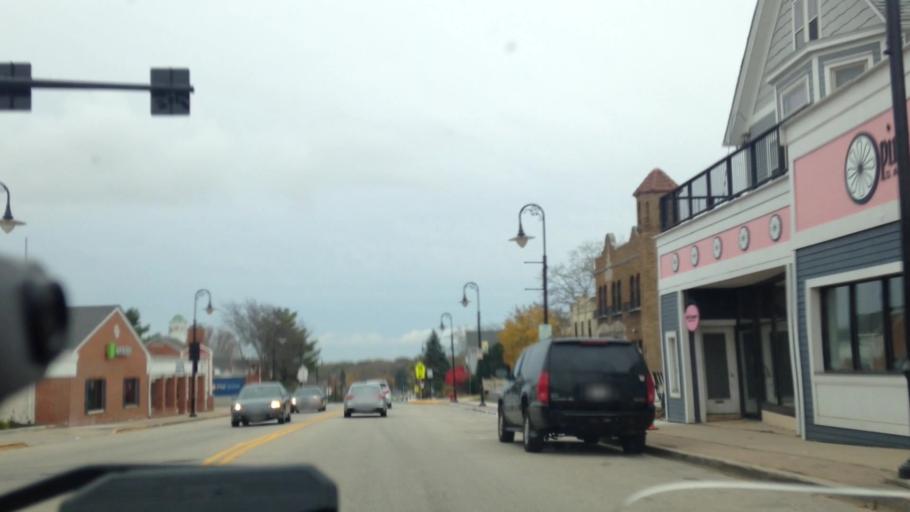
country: US
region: Wisconsin
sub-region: Waukesha County
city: Menomonee Falls
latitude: 43.1784
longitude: -88.1168
